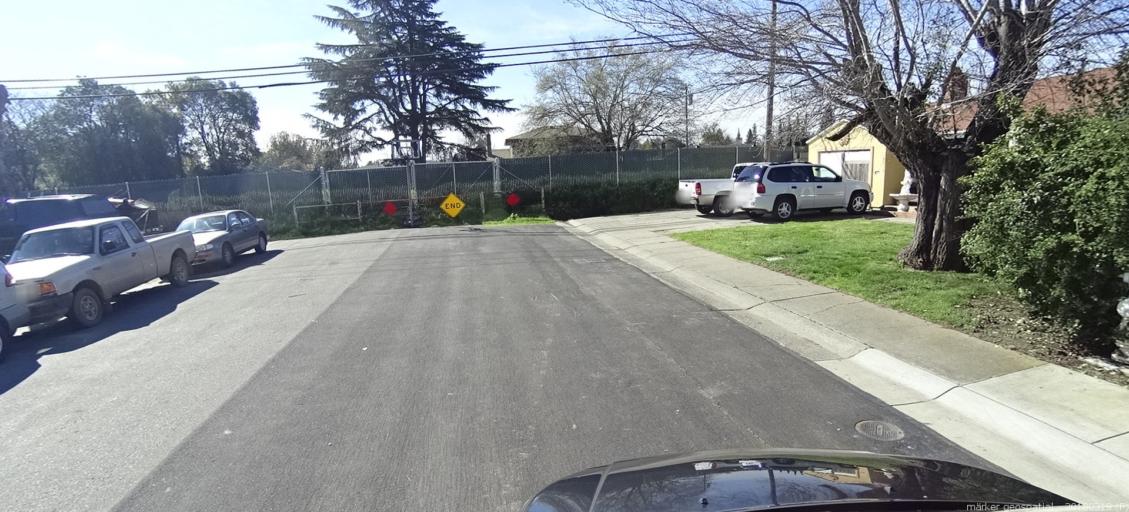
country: US
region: California
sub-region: Sacramento County
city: Parkway
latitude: 38.4852
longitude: -121.4414
